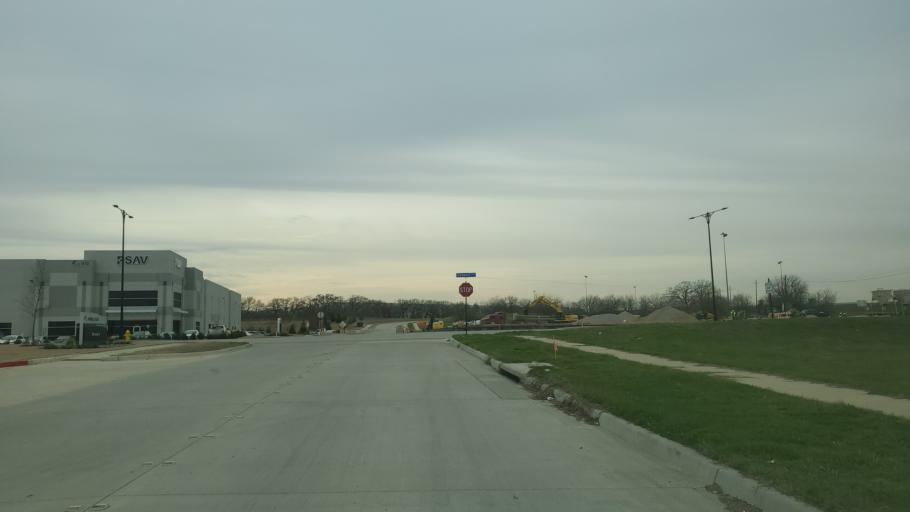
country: US
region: Texas
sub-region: Dallas County
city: Coppell
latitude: 32.9796
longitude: -97.0182
